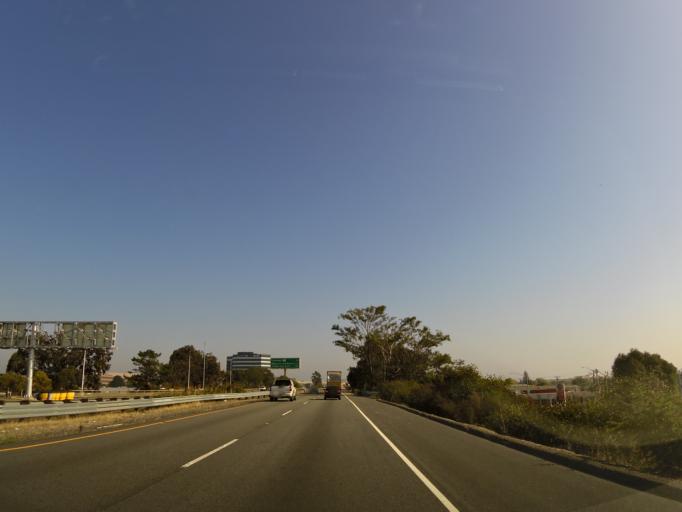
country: US
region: California
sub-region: San Mateo County
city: San Mateo
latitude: 37.5525
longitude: -122.3065
